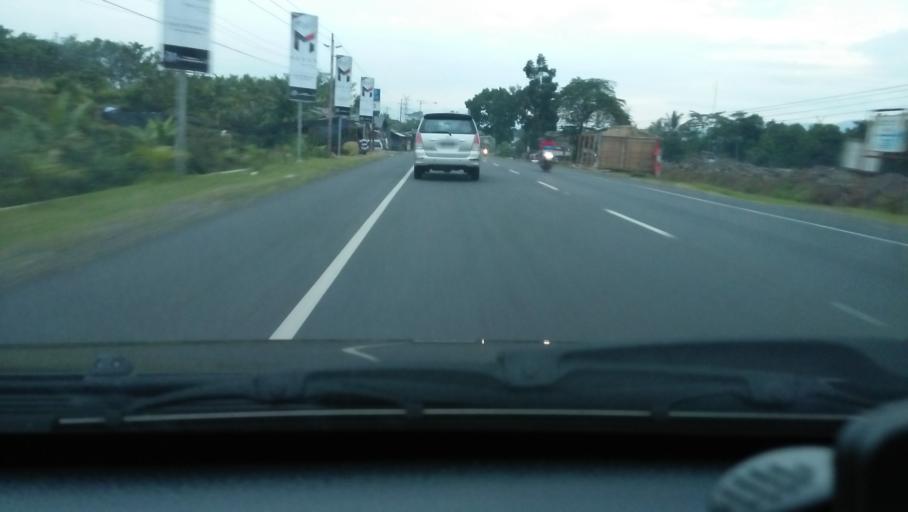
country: ID
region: Central Java
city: Magelang
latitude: -7.4121
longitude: 110.2364
